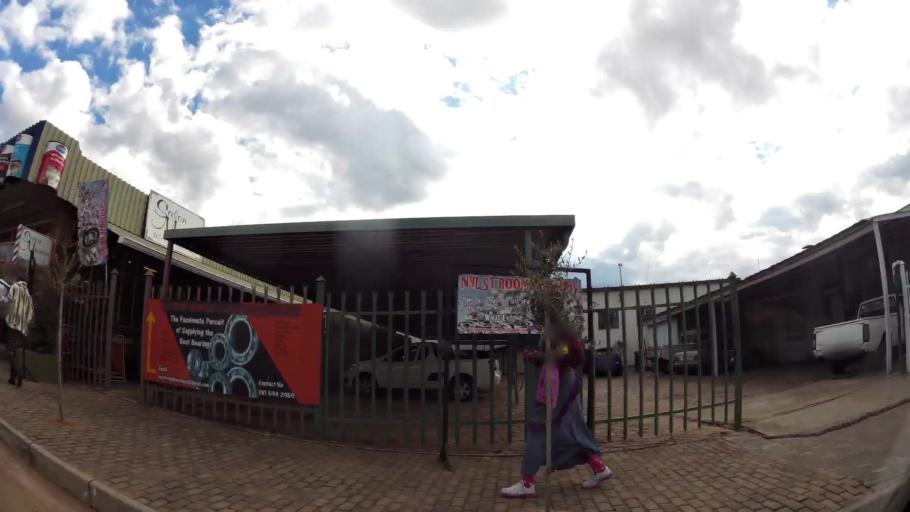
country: ZA
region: Limpopo
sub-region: Waterberg District Municipality
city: Modimolle
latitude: -24.7018
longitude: 28.4069
